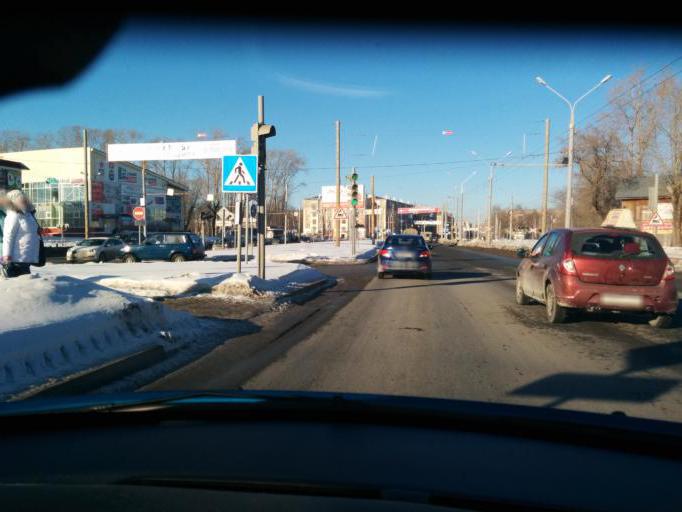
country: RU
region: Perm
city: Perm
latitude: 57.9834
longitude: 56.2586
